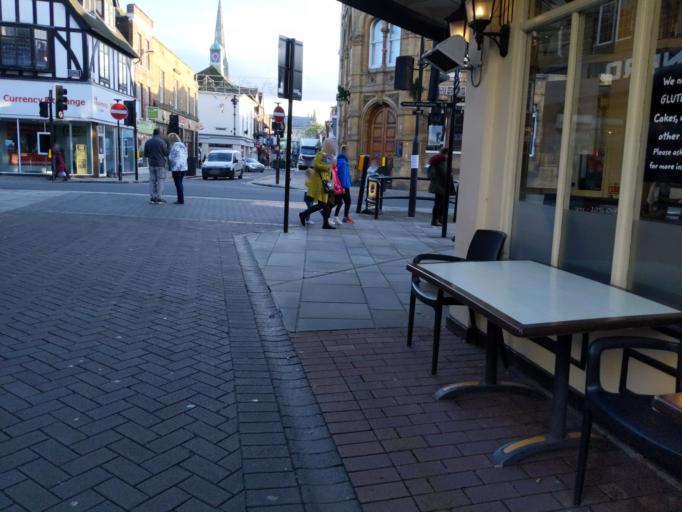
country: GB
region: England
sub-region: Wiltshire
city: Salisbury
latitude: 51.0688
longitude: -1.7972
